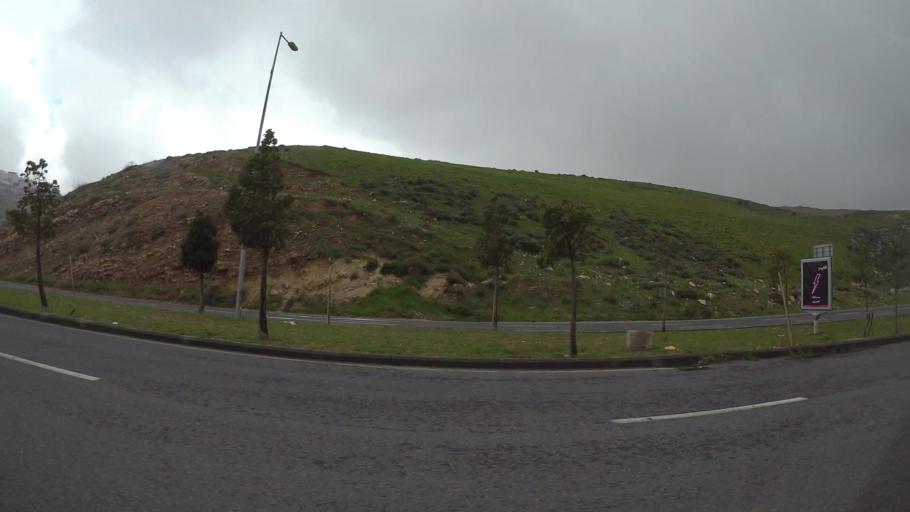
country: JO
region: Amman
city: Al Bunayyat ash Shamaliyah
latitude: 31.9299
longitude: 35.8778
